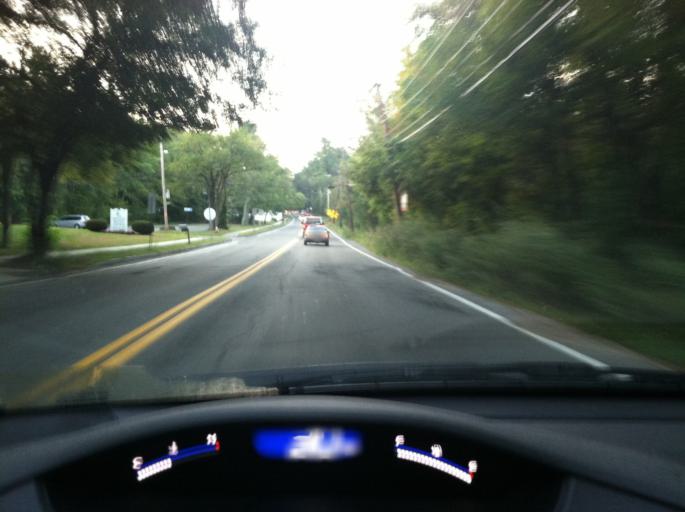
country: US
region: Massachusetts
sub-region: Middlesex County
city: Bedford
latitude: 42.4822
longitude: -71.2581
